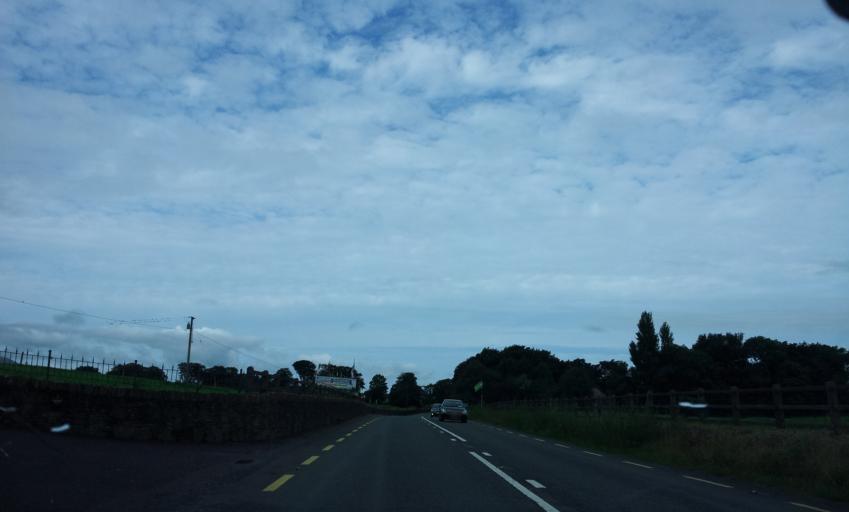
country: IE
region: Munster
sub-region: Ciarrai
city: Cill Airne
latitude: 52.0719
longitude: -9.6073
